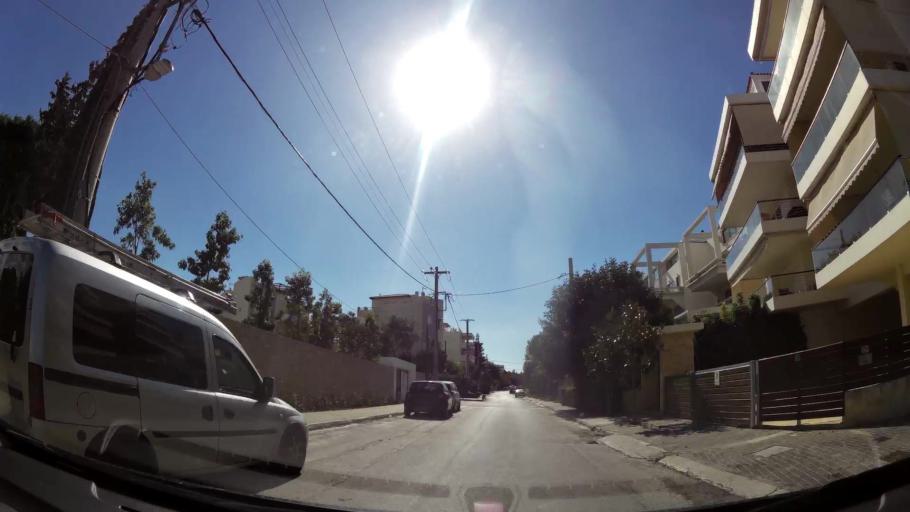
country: GR
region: Attica
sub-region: Nomarchia Anatolikis Attikis
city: Voula
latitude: 37.8285
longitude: 23.7763
